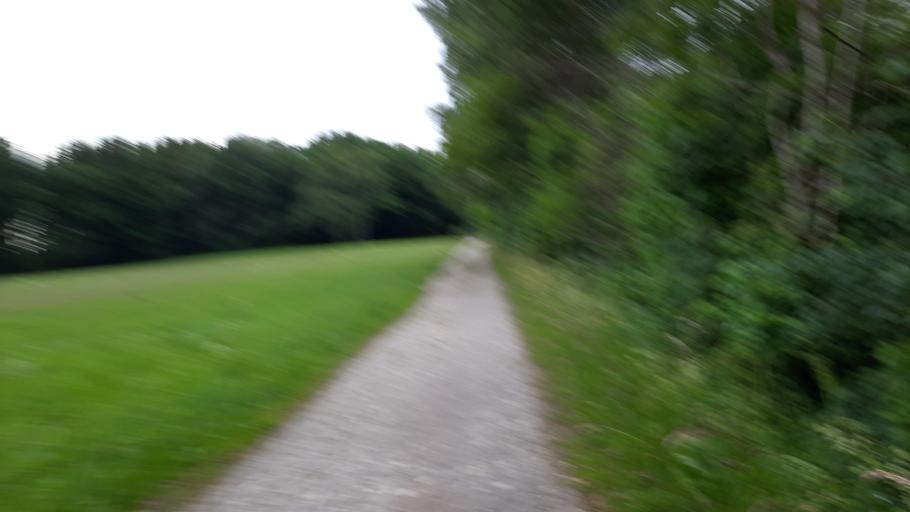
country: DE
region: Bavaria
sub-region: Upper Bavaria
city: Weyarn
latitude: 47.8482
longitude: 11.8423
